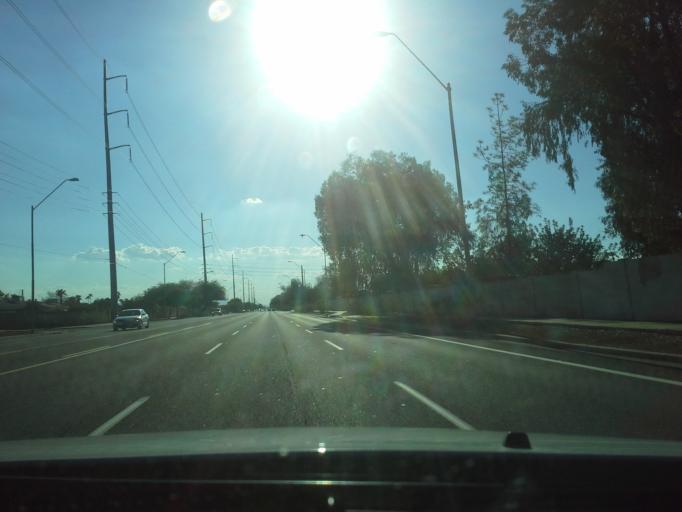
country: US
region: Arizona
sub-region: Maricopa County
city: Glendale
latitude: 33.6547
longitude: -112.1230
